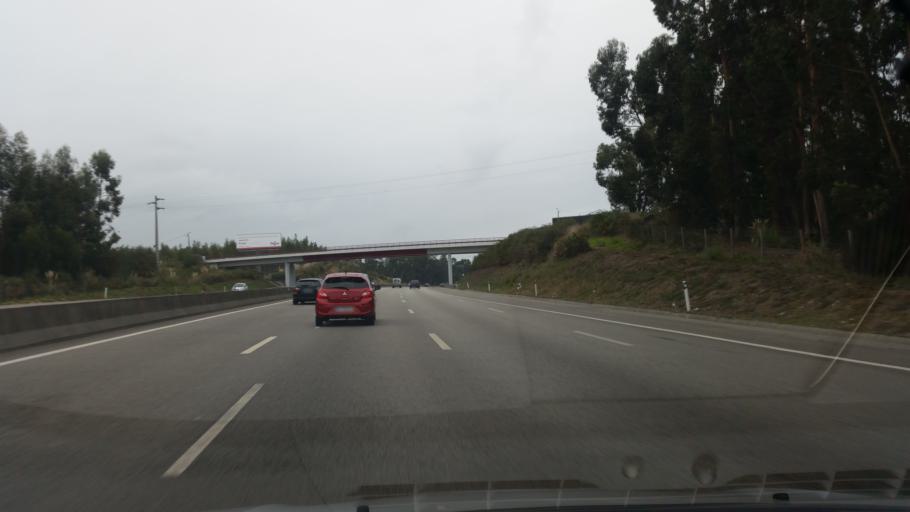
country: PT
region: Porto
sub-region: Maia
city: Nogueira
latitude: 41.2511
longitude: -8.5682
